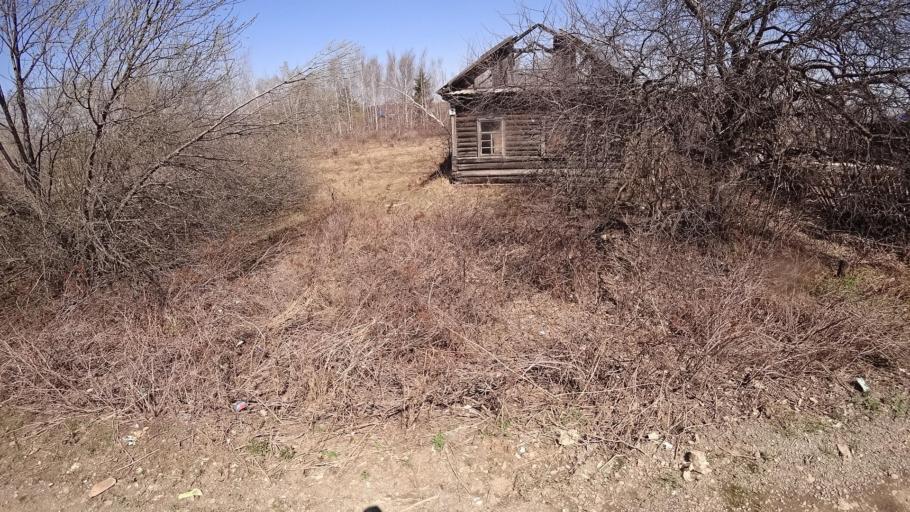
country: RU
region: Khabarovsk Krai
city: Khurba
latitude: 50.4101
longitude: 136.8646
